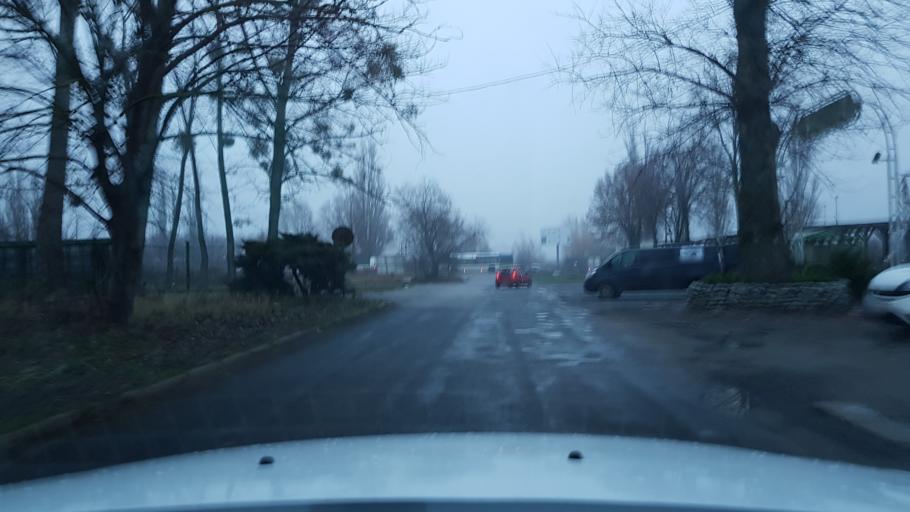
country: PL
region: West Pomeranian Voivodeship
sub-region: Powiat policki
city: Przeclaw
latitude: 53.3914
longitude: 14.4961
